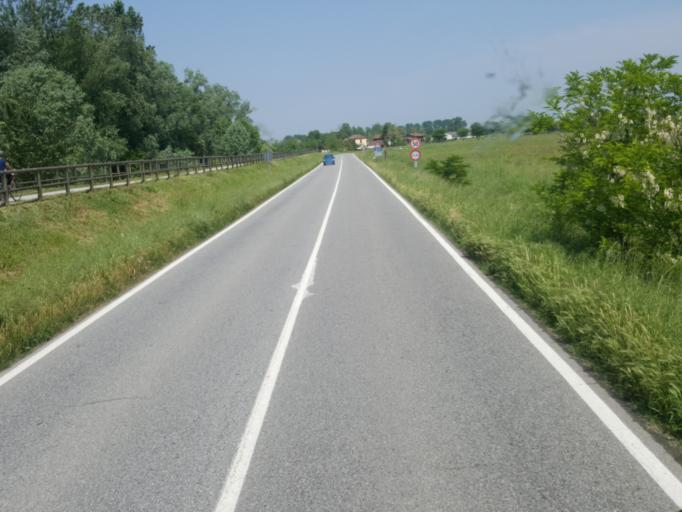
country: IT
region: Lombardy
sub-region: Provincia di Lodi
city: Lodi
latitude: 45.3260
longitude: 9.5107
